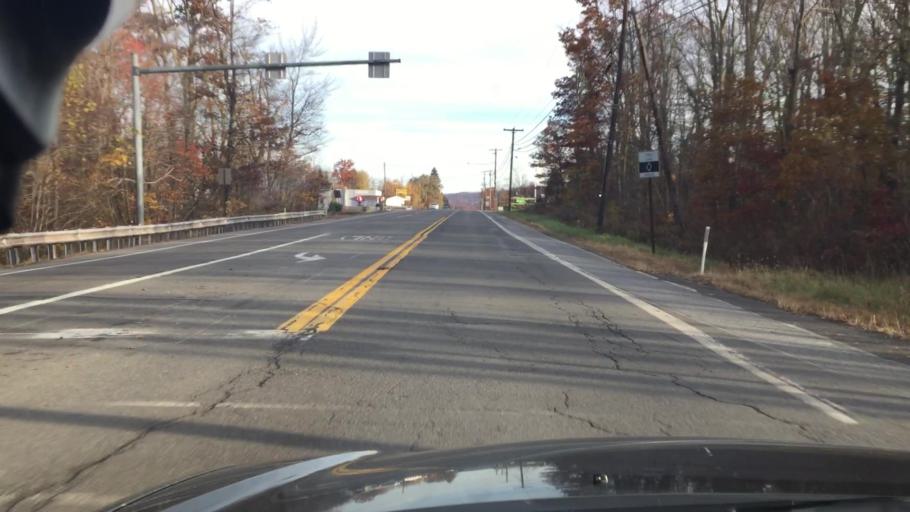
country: US
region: Pennsylvania
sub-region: Luzerne County
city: Mountain Top
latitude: 41.1333
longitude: -75.9043
